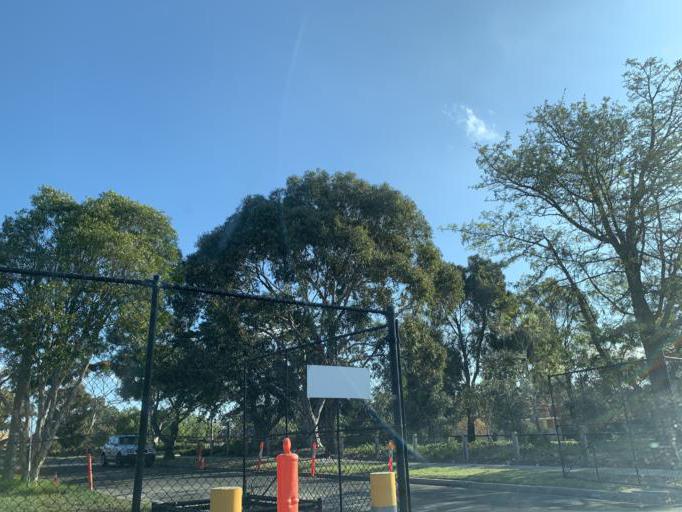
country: AU
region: Victoria
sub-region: Kingston
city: Mordialloc
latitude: -37.9910
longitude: 145.0949
